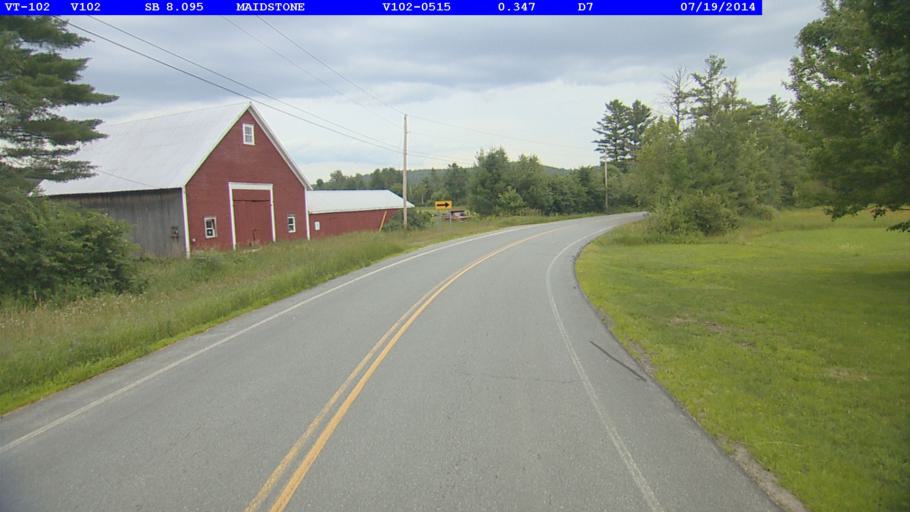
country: US
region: Vermont
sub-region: Essex County
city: Guildhall
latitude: 44.5758
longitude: -71.5542
